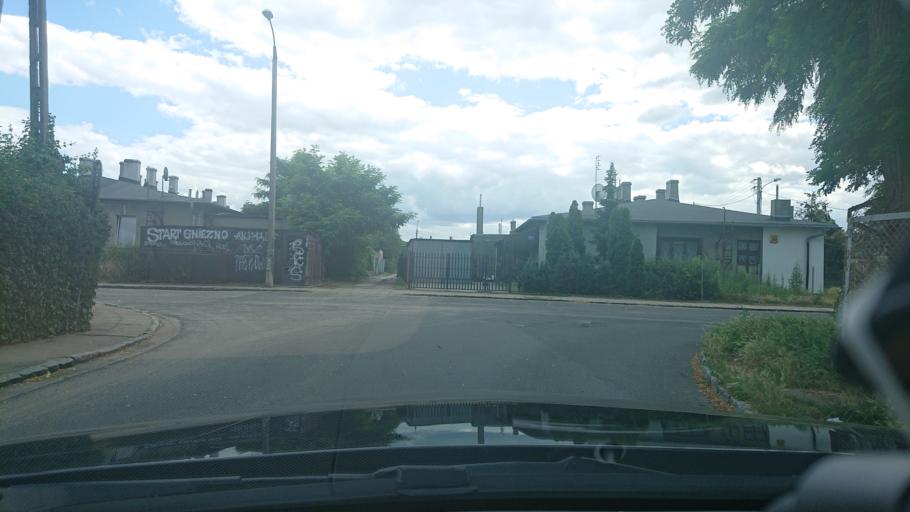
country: PL
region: Greater Poland Voivodeship
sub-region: Powiat gnieznienski
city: Gniezno
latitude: 52.5156
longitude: 17.6064
